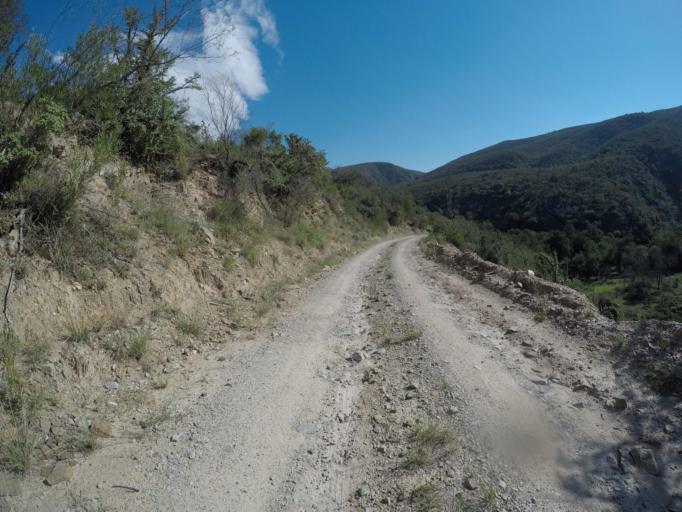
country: ZA
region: Eastern Cape
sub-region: Cacadu District Municipality
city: Kareedouw
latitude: -33.6465
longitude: 24.4535
